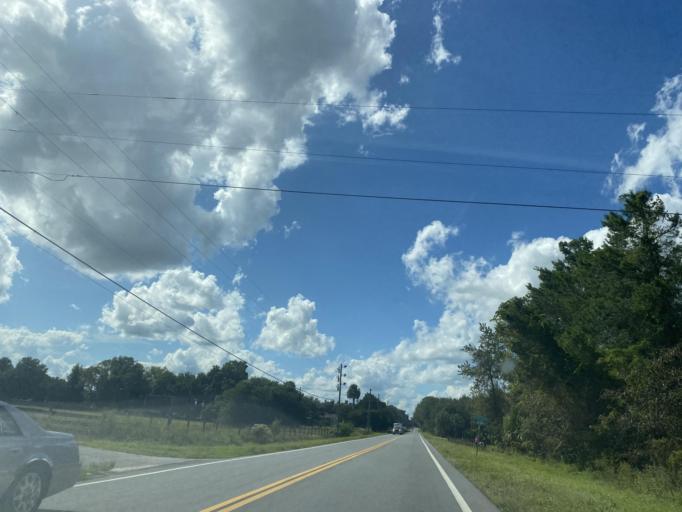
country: US
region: Florida
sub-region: Sumter County
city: The Villages
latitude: 28.9821
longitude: -81.9608
